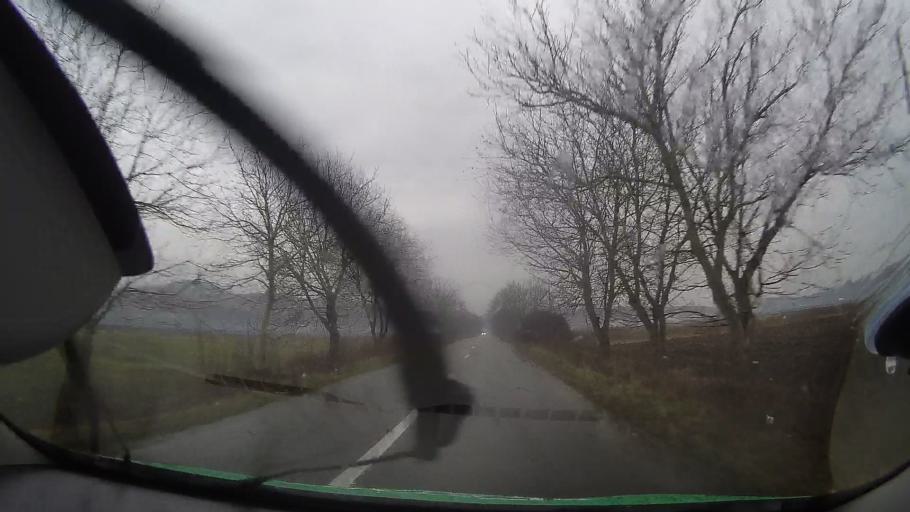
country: RO
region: Bihor
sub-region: Comuna Uileacu de Beius
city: Uileacu de Beius
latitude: 46.6810
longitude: 22.2428
